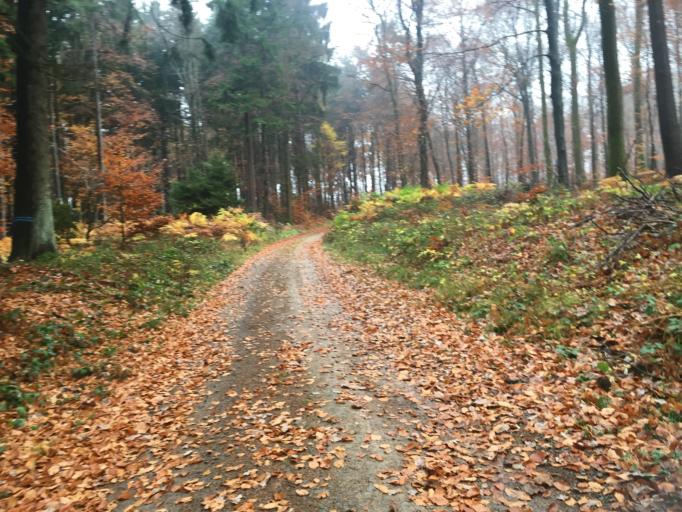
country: DE
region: Hesse
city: Neckarsteinach
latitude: 49.4449
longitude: 8.8520
